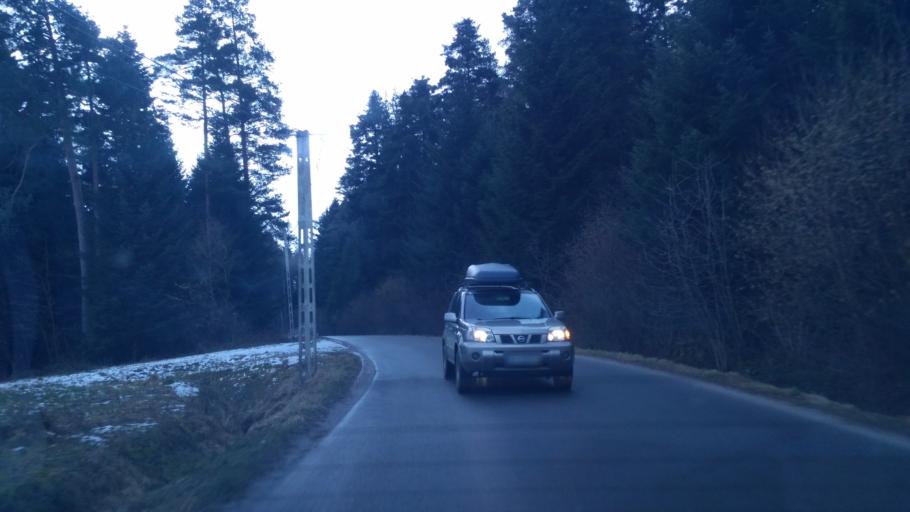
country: PL
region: Subcarpathian Voivodeship
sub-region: Powiat rzeszowski
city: Blazowa
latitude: 49.8592
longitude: 22.0966
